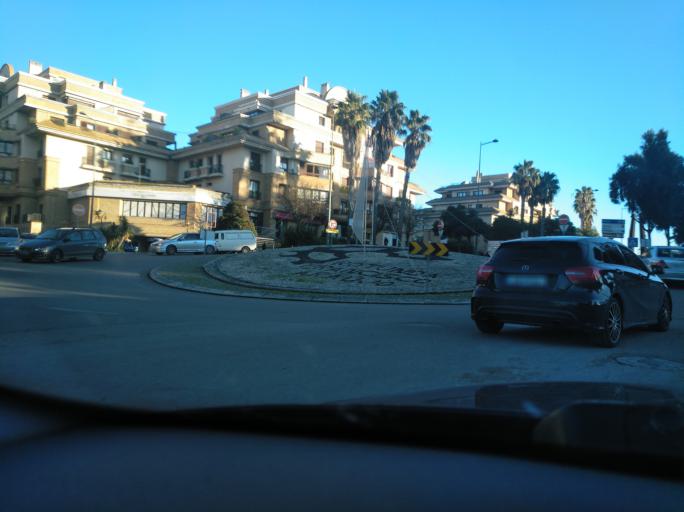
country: PT
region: Lisbon
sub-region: Loures
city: Sacavem
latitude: 38.7942
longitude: -9.1044
